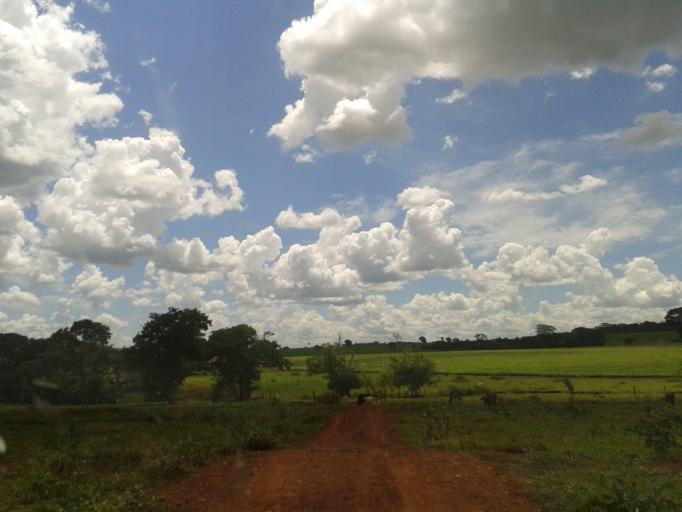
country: BR
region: Minas Gerais
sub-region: Capinopolis
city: Capinopolis
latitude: -18.7846
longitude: -49.8134
